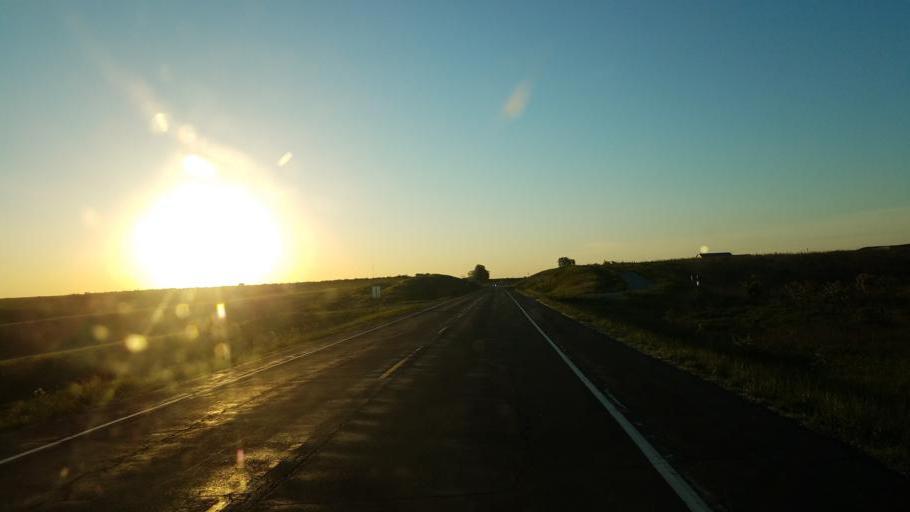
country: US
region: Missouri
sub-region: Schuyler County
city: Lancaster
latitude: 40.4928
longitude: -92.5626
